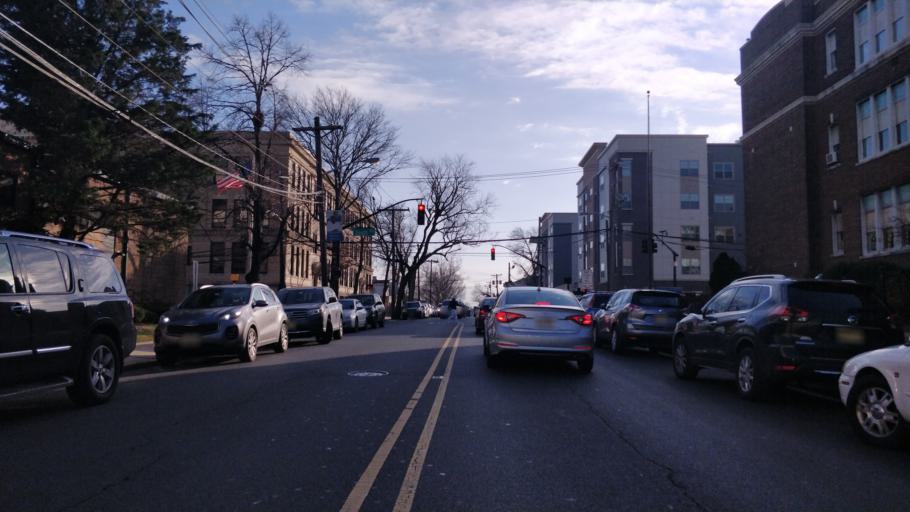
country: US
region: New Jersey
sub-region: Union County
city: Elizabeth
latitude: 40.6582
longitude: -74.2154
